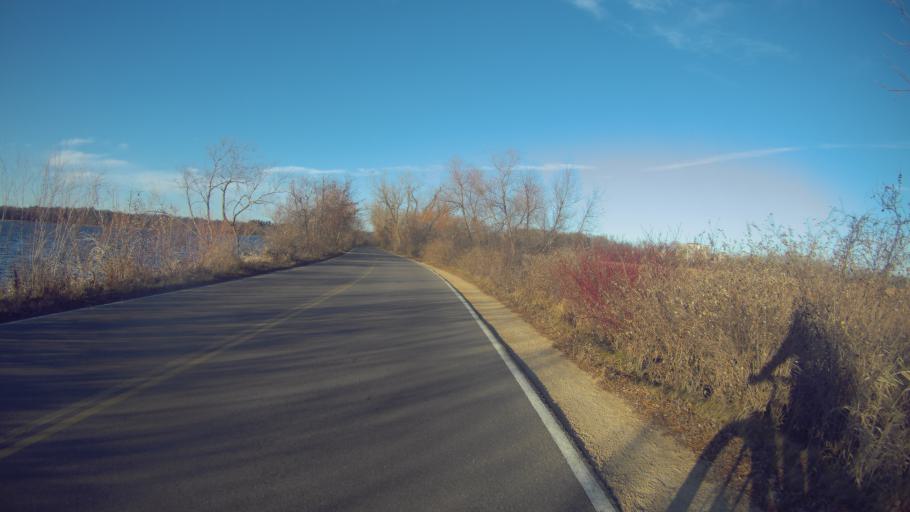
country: US
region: Wisconsin
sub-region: Dane County
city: Madison
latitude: 43.0527
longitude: -89.4093
